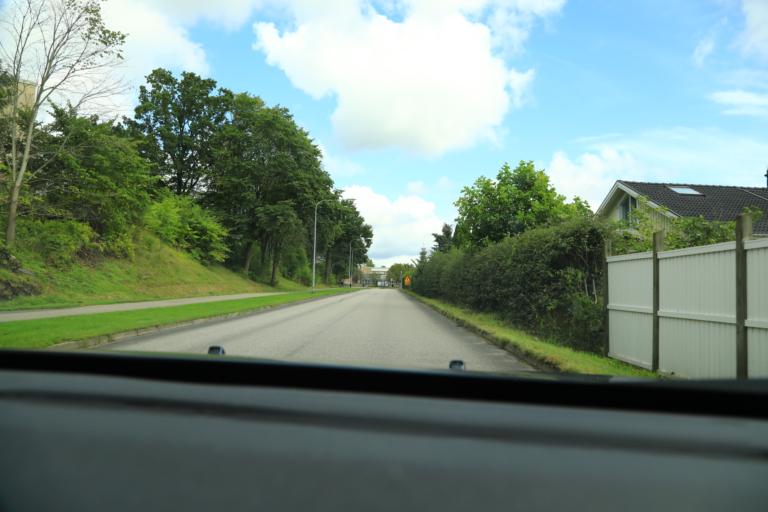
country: SE
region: Halland
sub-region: Kungsbacka Kommun
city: Kungsbacka
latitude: 57.4934
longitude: 12.0848
